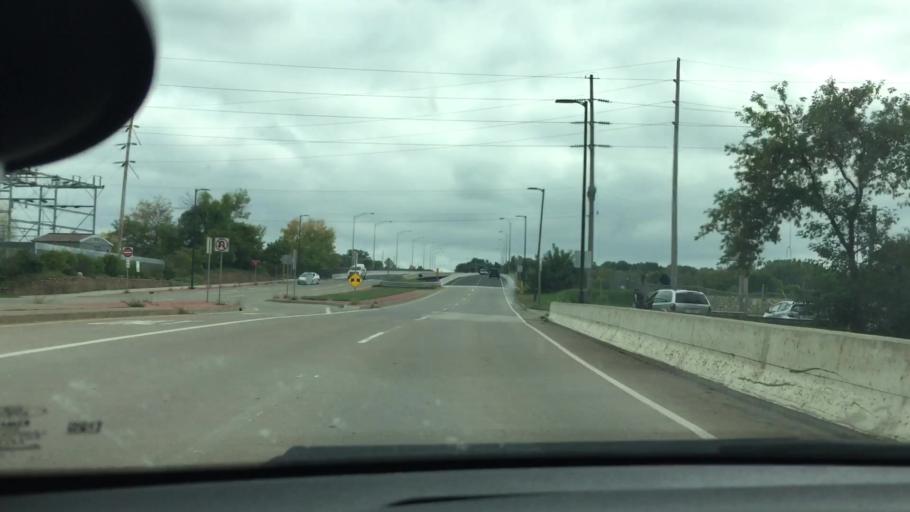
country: US
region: Wisconsin
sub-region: Chippewa County
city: Chippewa Falls
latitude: 44.9332
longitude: -91.3887
